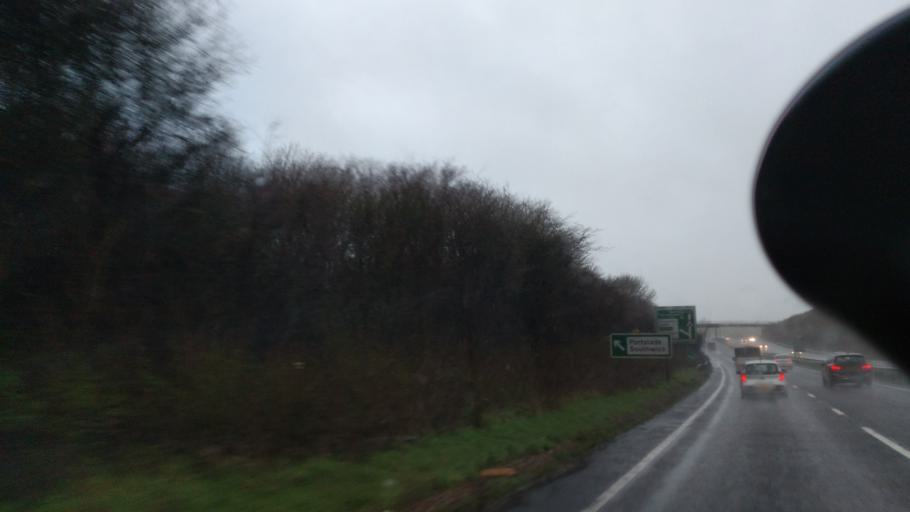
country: GB
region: England
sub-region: East Sussex
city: Portslade
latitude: 50.8555
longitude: -0.2025
